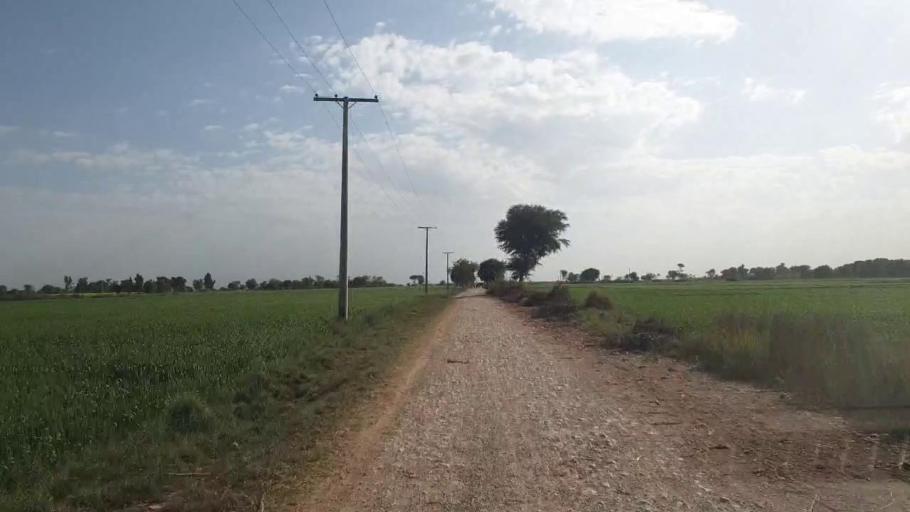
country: PK
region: Sindh
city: Shahdadpur
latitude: 26.0291
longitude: 68.4780
